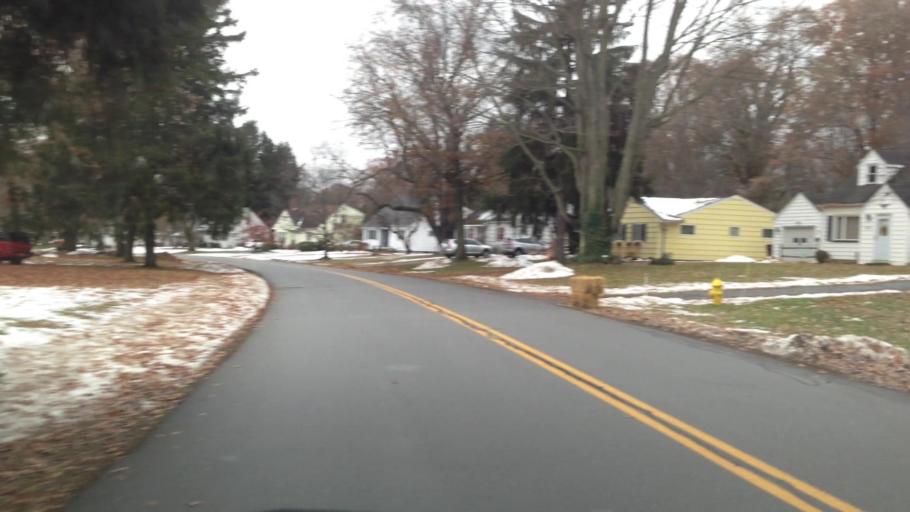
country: US
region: New York
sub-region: Monroe County
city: North Gates
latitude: 43.1240
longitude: -77.7244
